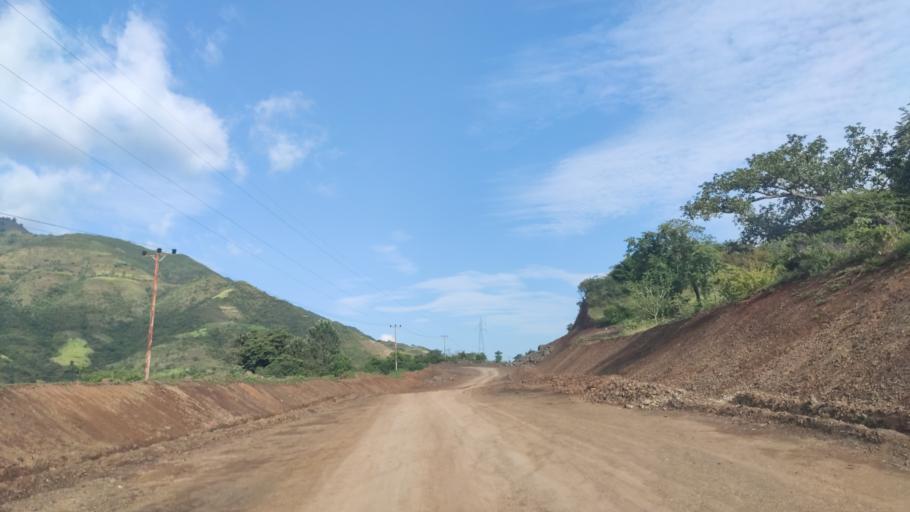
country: ET
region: Southern Nations, Nationalities, and People's Region
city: Arba Minch'
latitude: 6.4257
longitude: 37.3408
